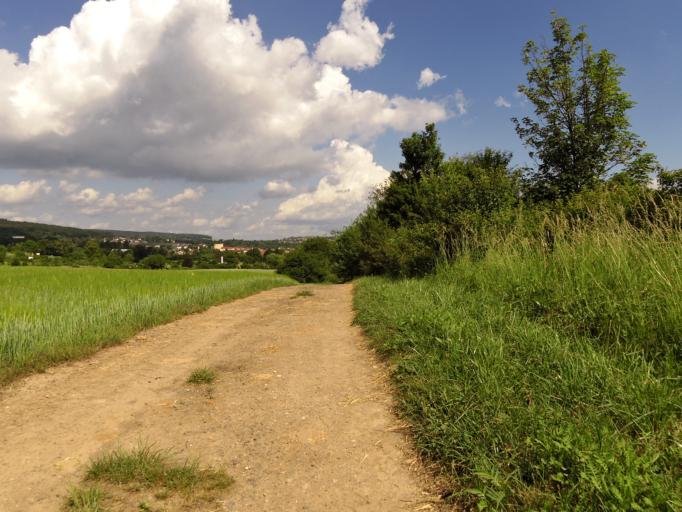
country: DE
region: Rheinland-Pfalz
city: Eisenberg
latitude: 49.5513
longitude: 8.0773
